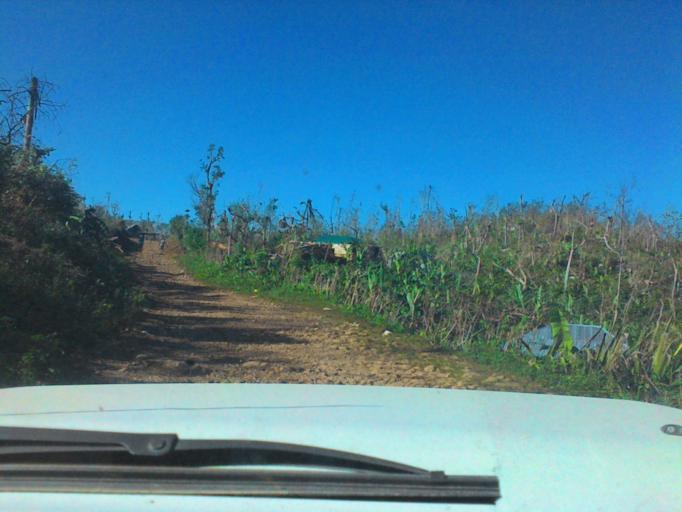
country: HT
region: Grandans
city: Jeremie
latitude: 18.4898
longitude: -74.1094
